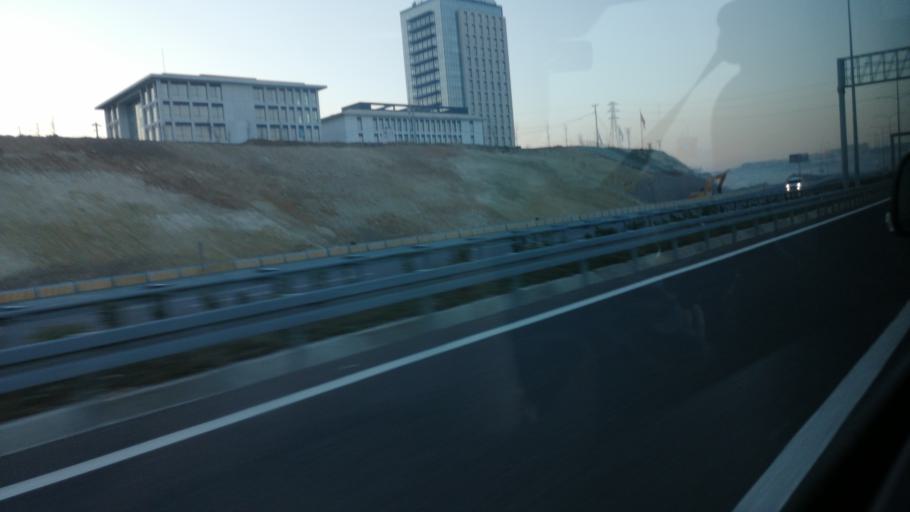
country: TR
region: Kocaeli
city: Tavsanli
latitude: 40.7913
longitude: 29.5135
